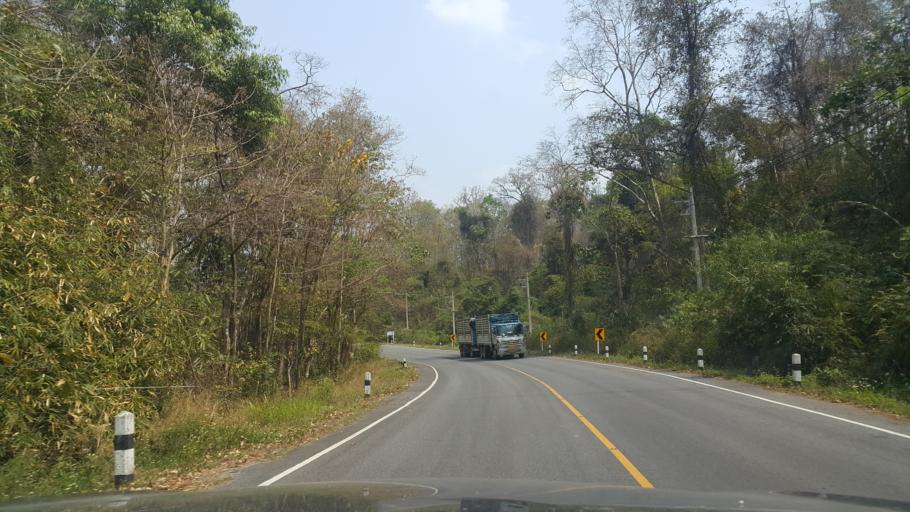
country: TH
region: Lamphun
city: Thung Hua Chang
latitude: 17.9058
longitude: 99.1430
